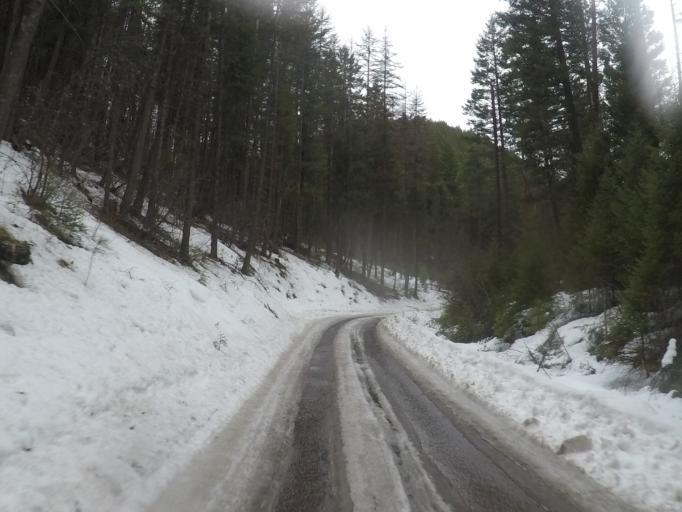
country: US
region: Montana
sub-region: Missoula County
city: East Missoula
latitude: 46.9251
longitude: -113.9632
